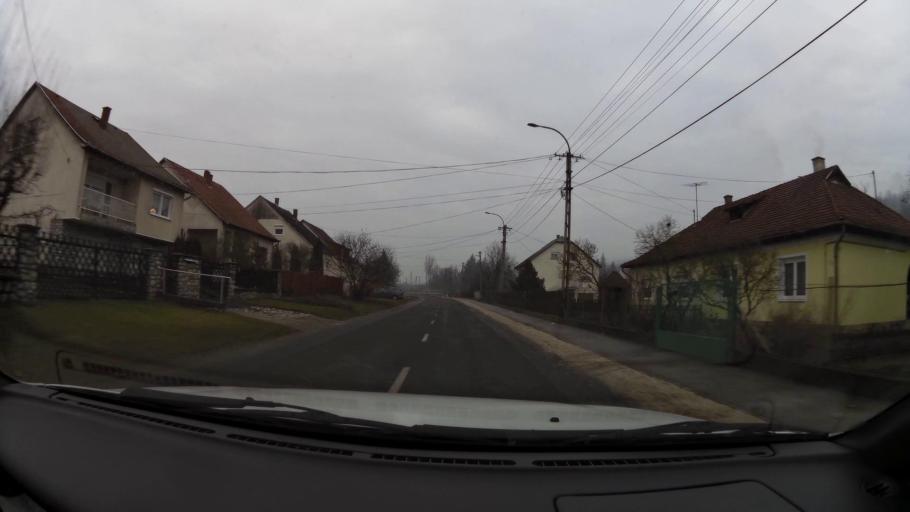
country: HU
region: Borsod-Abauj-Zemplen
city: Izsofalva
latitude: 48.3350
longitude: 20.6490
